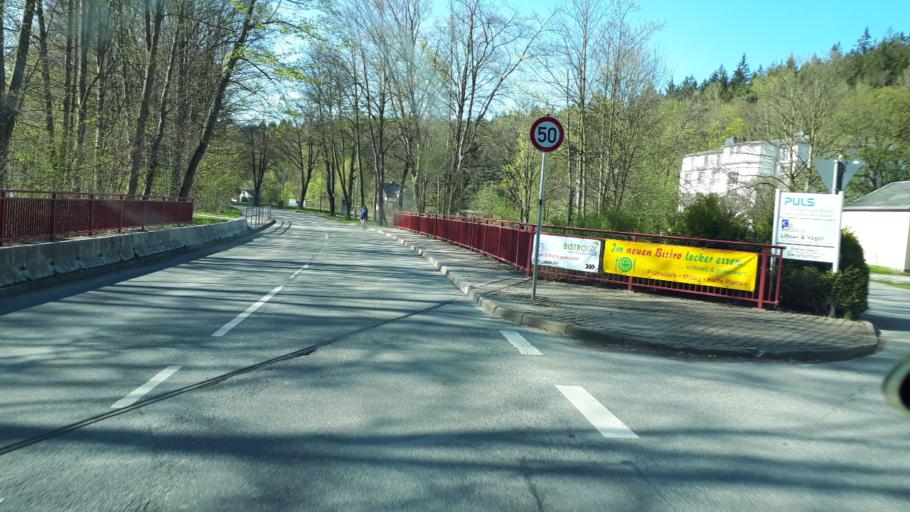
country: DE
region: Saxony
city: Chemnitz
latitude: 50.7826
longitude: 12.9719
